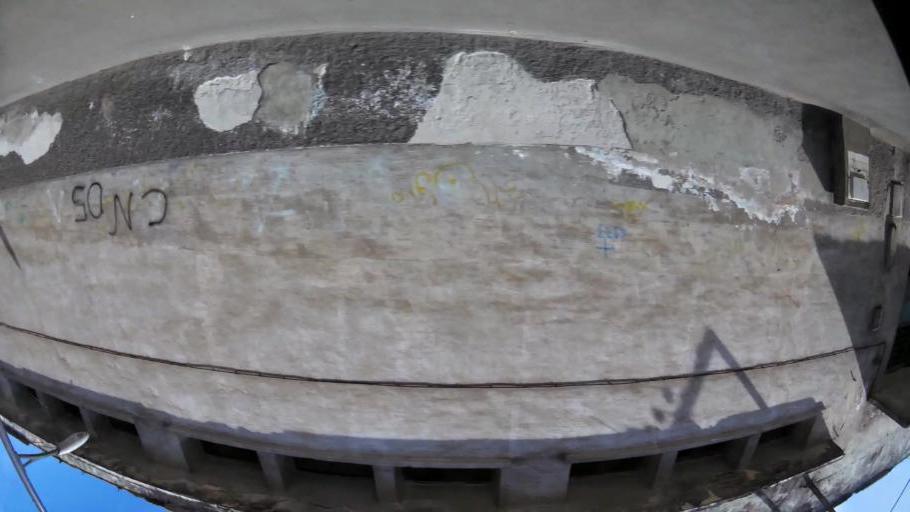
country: MA
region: Grand Casablanca
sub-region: Casablanca
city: Casablanca
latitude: 33.5924
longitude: -7.5814
